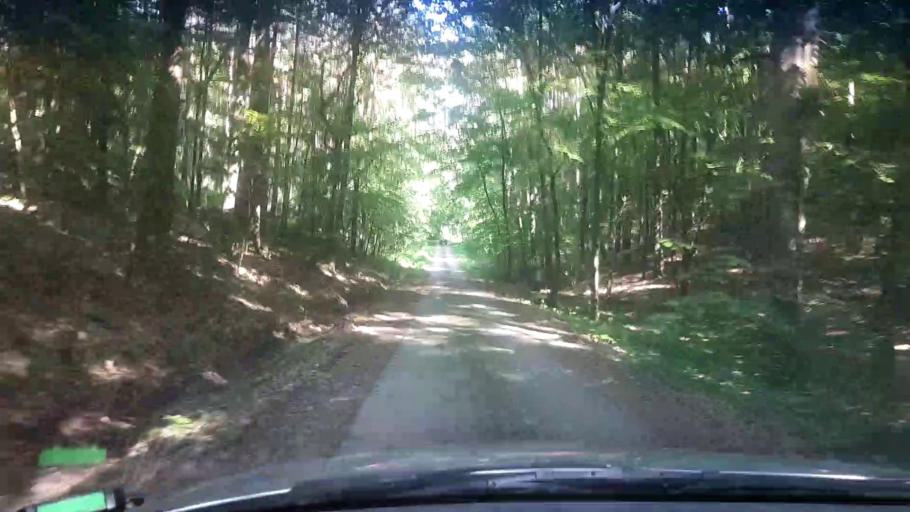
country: DE
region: Bavaria
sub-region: Upper Franconia
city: Lauter
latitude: 49.9446
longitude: 10.7849
